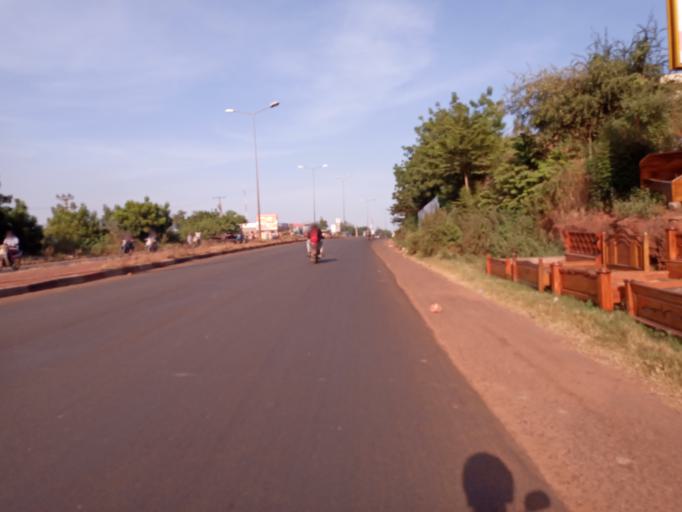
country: ML
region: Bamako
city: Bamako
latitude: 12.6168
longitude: -7.9875
